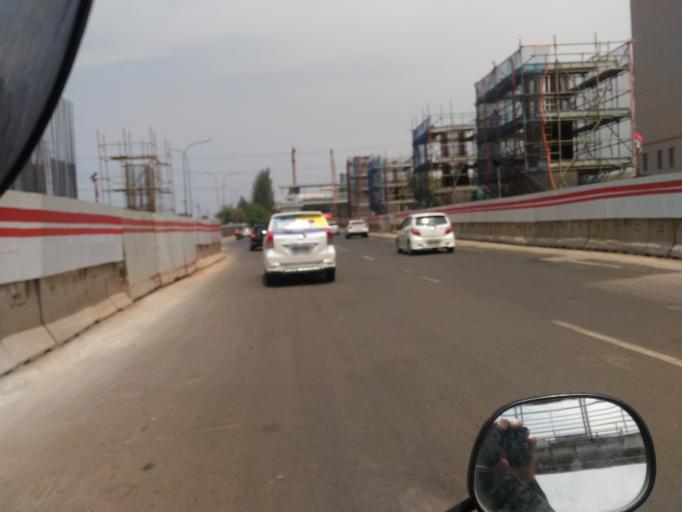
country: ID
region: Jakarta Raya
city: Jakarta
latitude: -6.2460
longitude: 106.8723
